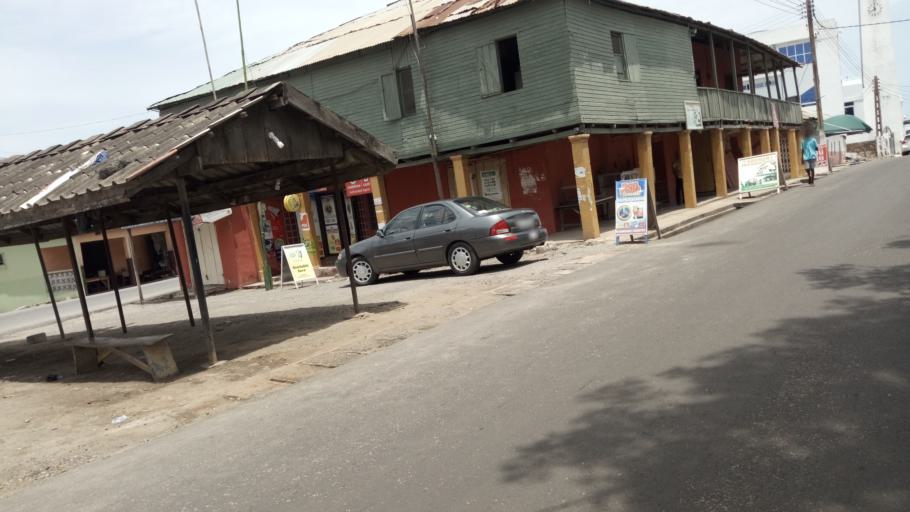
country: GH
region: Central
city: Winneba
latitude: 5.3410
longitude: -0.6241
